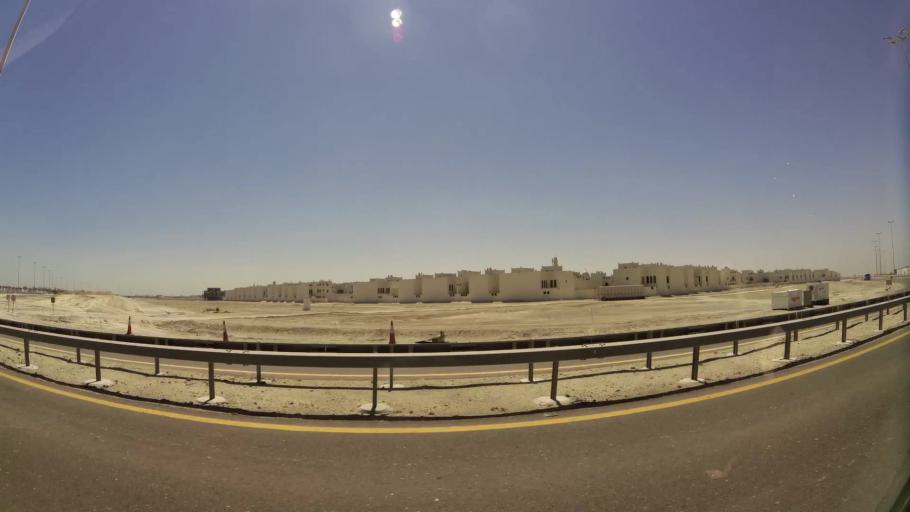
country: BH
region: Muharraq
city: Al Muharraq
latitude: 26.3045
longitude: 50.6396
